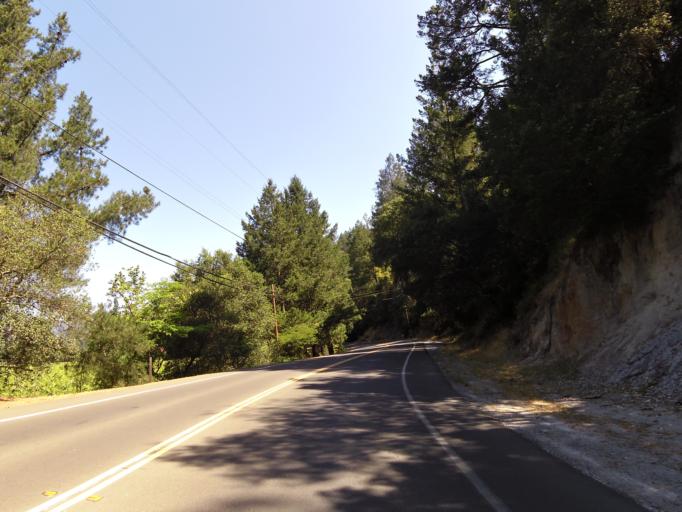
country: US
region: California
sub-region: Napa County
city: Deer Park
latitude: 38.5306
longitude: -122.4908
